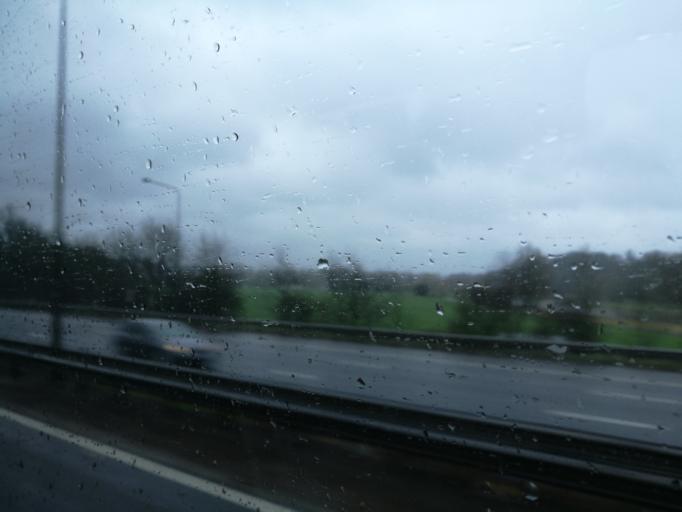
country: GB
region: England
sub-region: Hertfordshire
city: Watford
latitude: 51.6769
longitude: -0.3737
